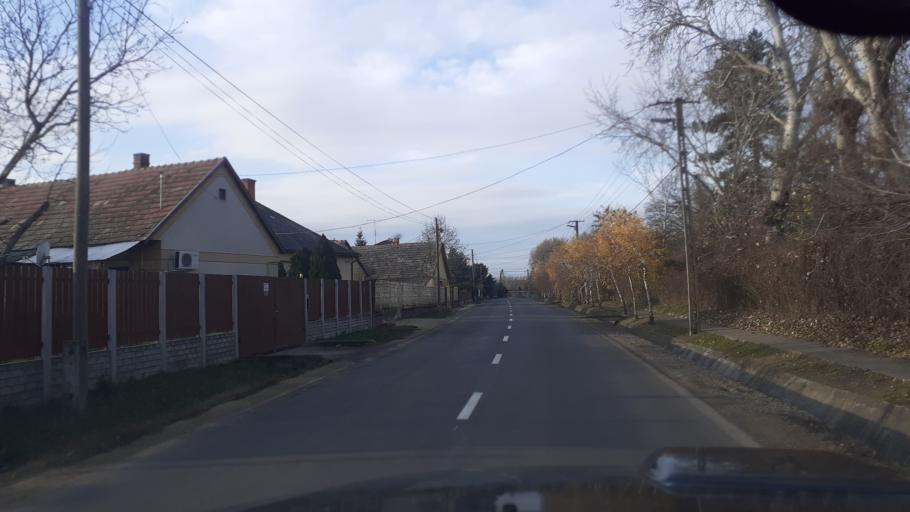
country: HU
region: Bacs-Kiskun
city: Tass
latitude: 47.0233
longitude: 19.0276
